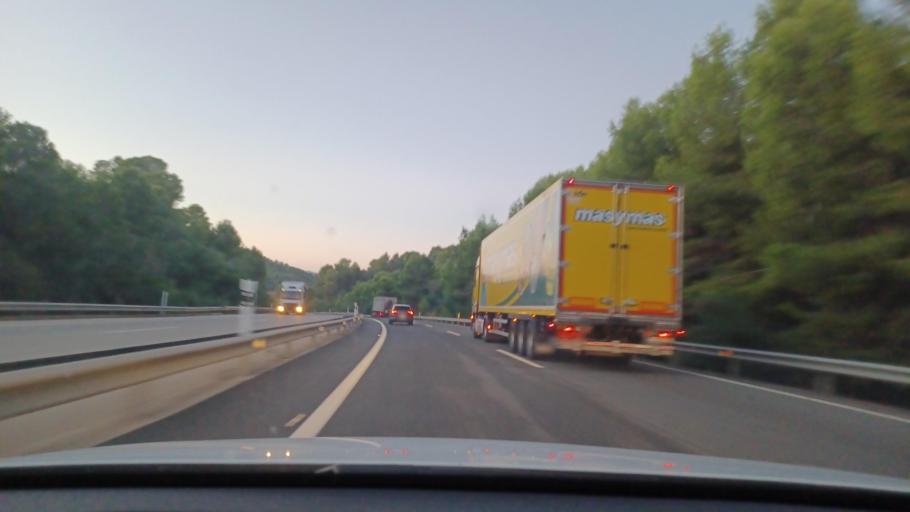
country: ES
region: Valencia
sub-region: Provincia de Valencia
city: Oliva
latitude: 38.9119
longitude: -0.1301
